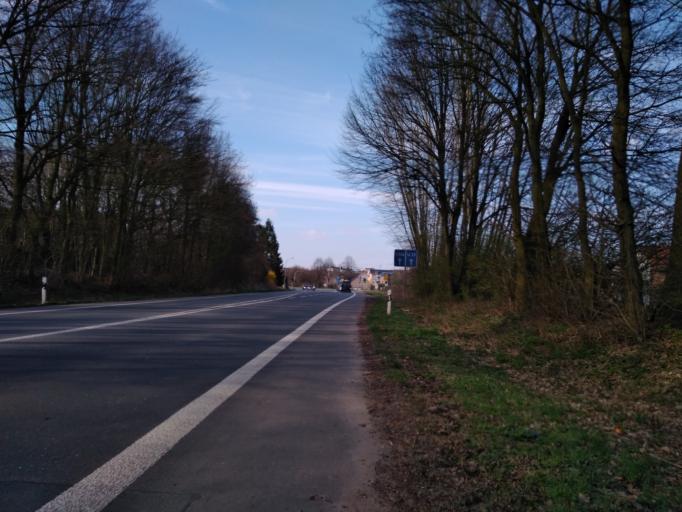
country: DE
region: North Rhine-Westphalia
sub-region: Regierungsbezirk Munster
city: Gladbeck
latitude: 51.5991
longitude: 6.9233
